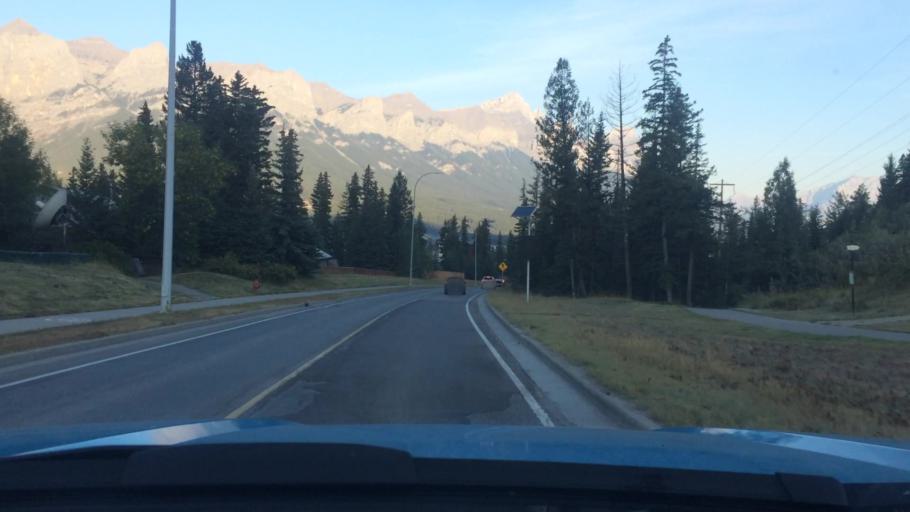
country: CA
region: Alberta
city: Canmore
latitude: 51.0876
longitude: -115.3333
